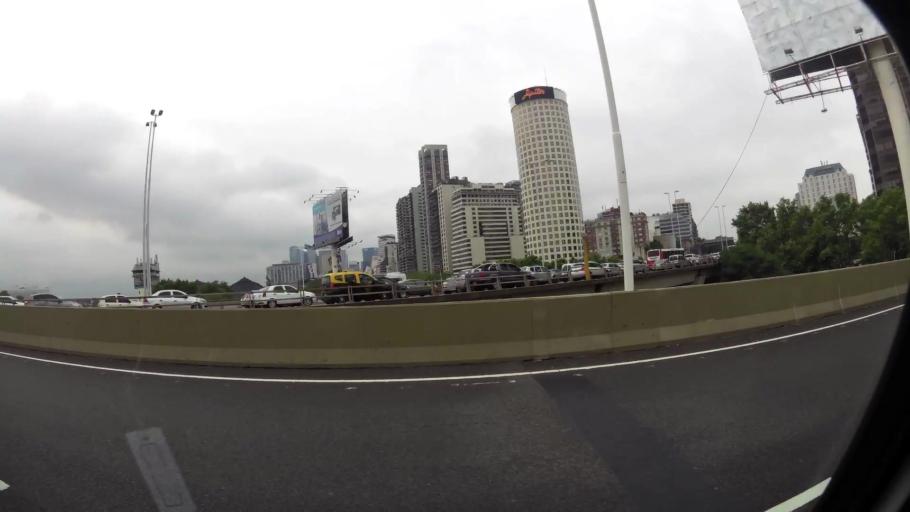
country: AR
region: Buenos Aires F.D.
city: Retiro
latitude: -34.5878
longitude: -58.3815
